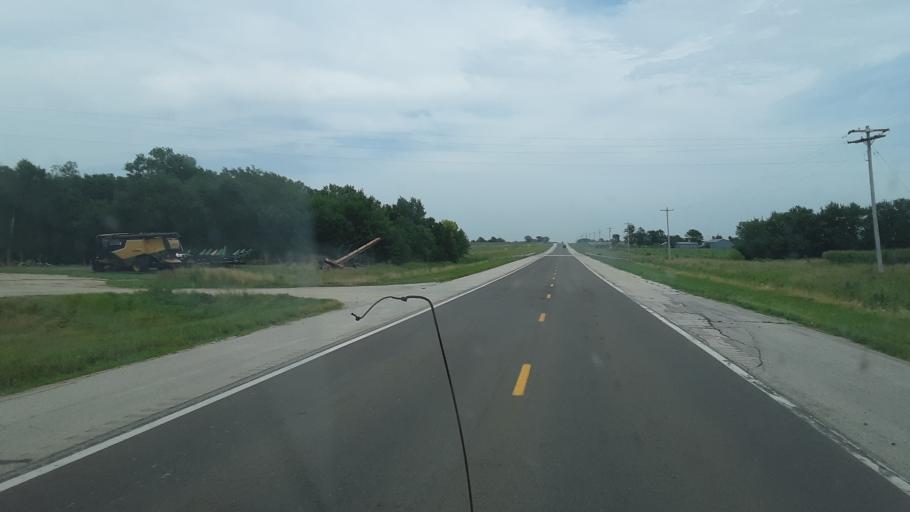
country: US
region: Kansas
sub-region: Allen County
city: Iola
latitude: 37.9226
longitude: -95.4759
